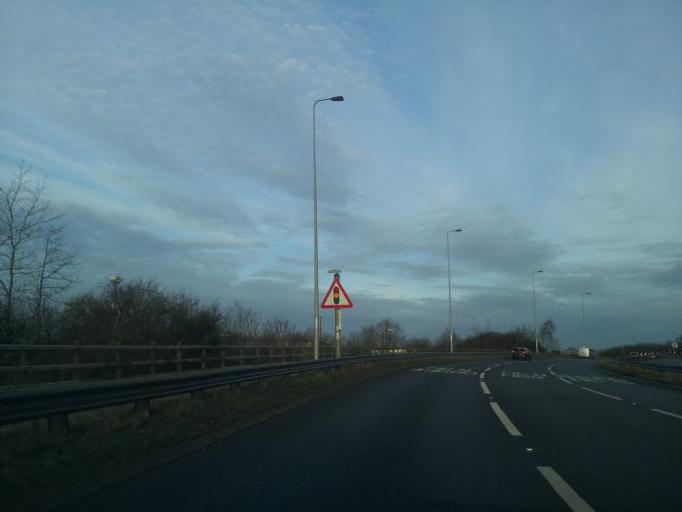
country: GB
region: England
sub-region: Warwickshire
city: Bedworth
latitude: 52.4359
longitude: -1.4286
